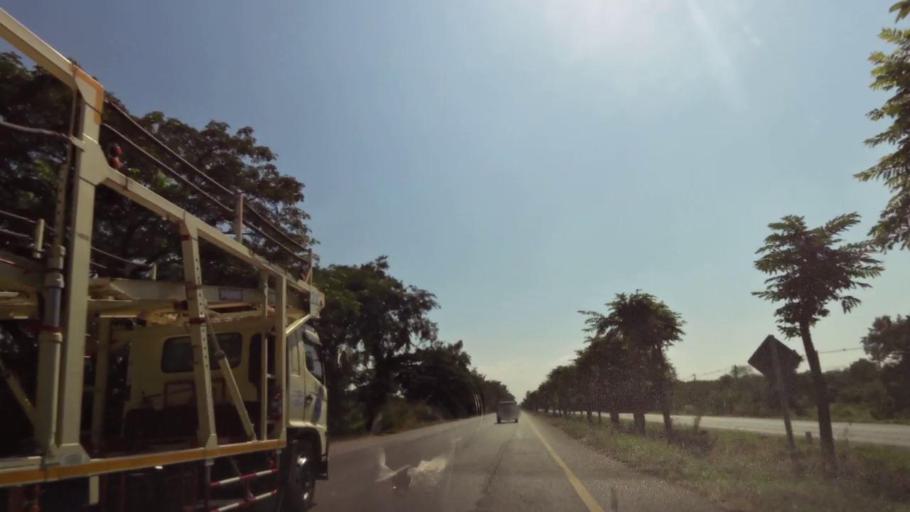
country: TH
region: Nakhon Sawan
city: Kao Liao
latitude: 15.7922
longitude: 100.1207
